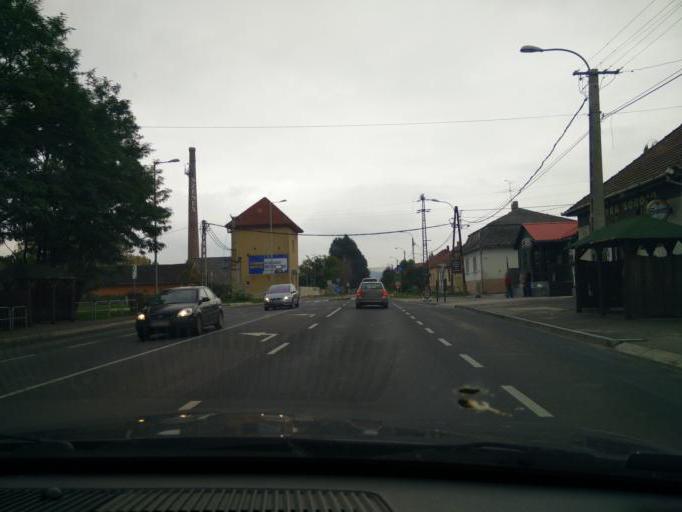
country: HU
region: Komarom-Esztergom
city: Kesztolc
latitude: 47.6878
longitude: 18.7713
